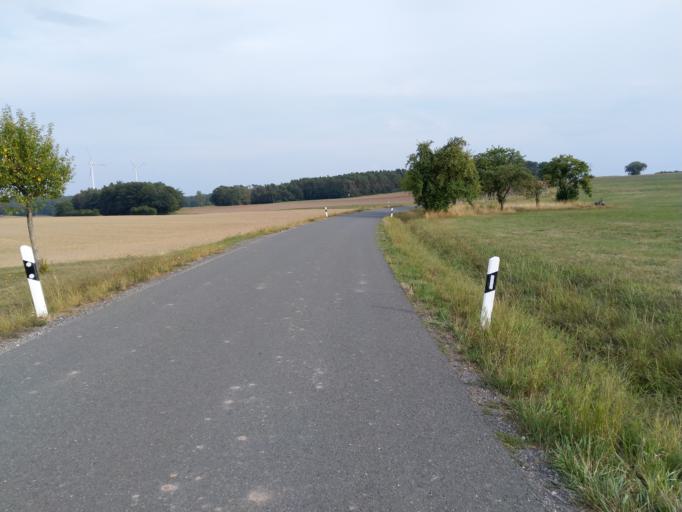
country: DE
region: Bavaria
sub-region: Regierungsbezirk Mittelfranken
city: Hagenbuchach
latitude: 49.5335
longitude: 10.7732
